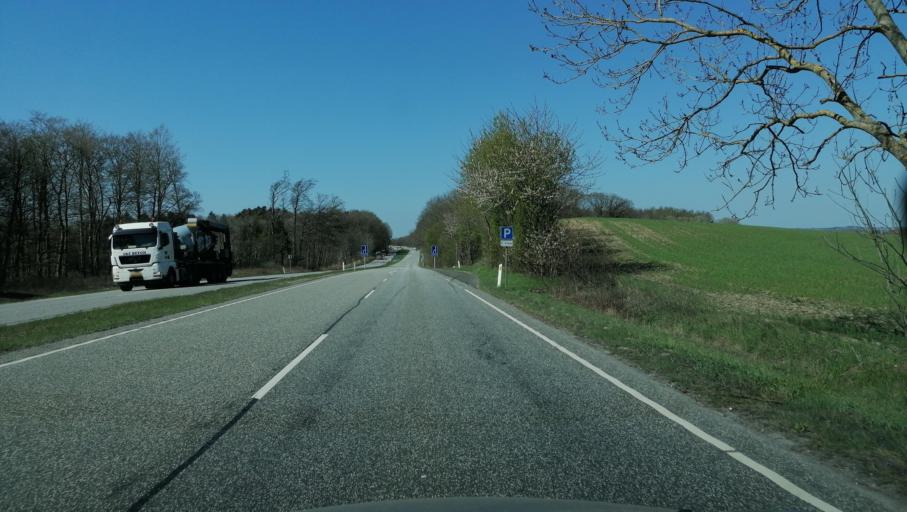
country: DK
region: Zealand
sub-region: Holbaek Kommune
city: Svinninge
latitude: 55.6553
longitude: 11.5446
